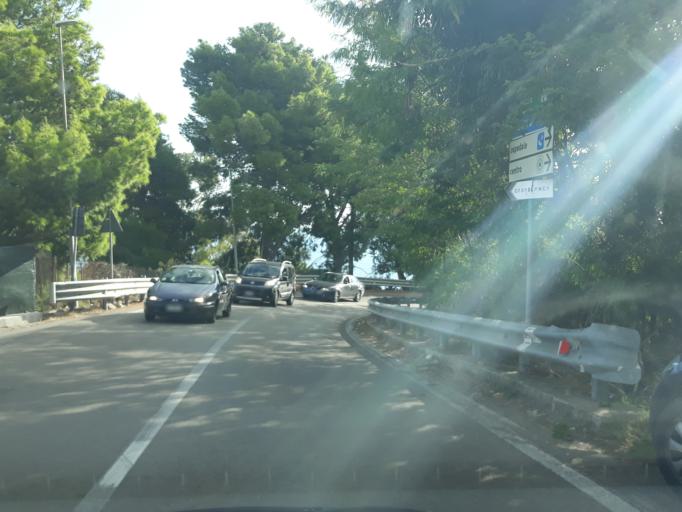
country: IT
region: Sicily
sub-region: Palermo
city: Cefalu
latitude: 38.0328
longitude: 14.0374
